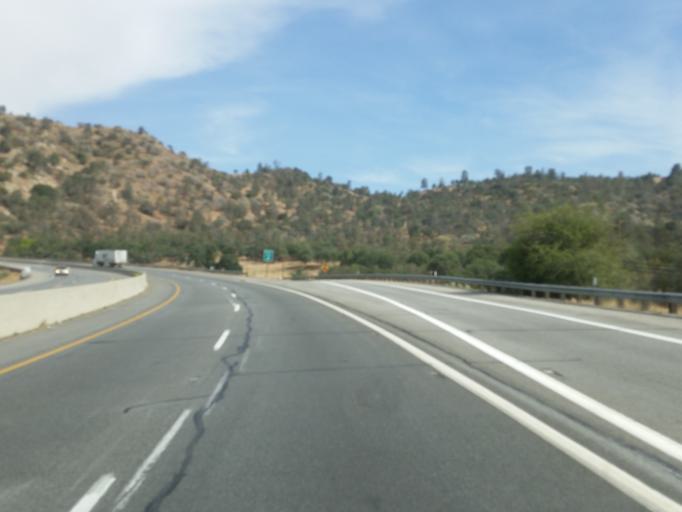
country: US
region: California
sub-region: Kern County
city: Bear Valley Springs
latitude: 35.2255
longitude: -118.5685
